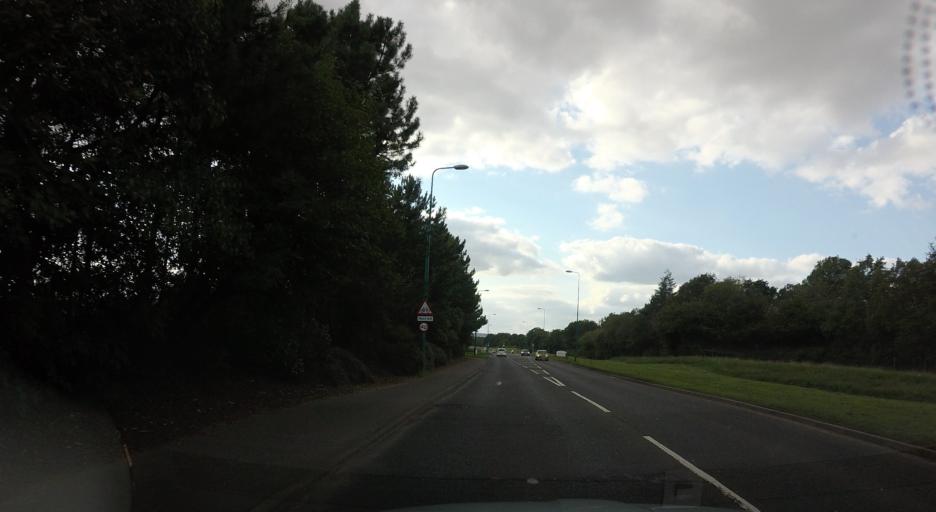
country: GB
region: Scotland
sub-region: Angus
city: Muirhead
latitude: 56.4557
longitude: -3.0326
